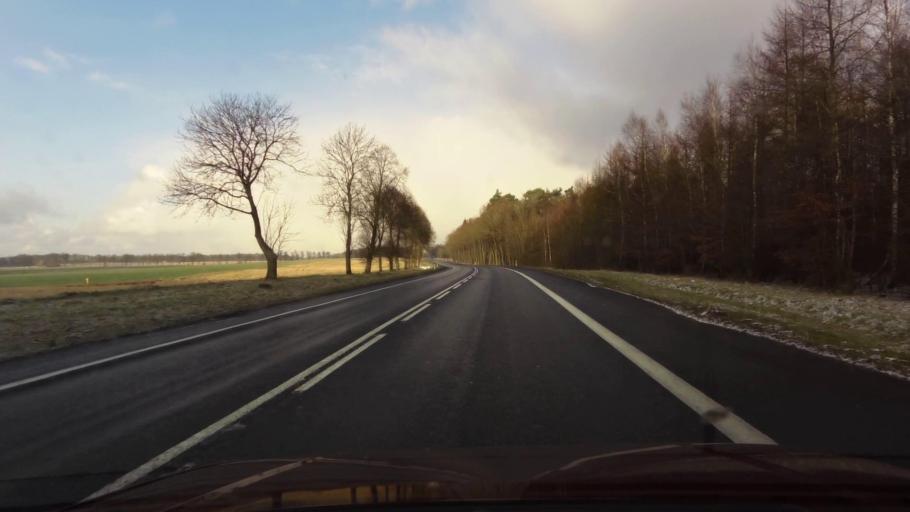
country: PL
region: West Pomeranian Voivodeship
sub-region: Powiat bialogardzki
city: Bialogard
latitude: 54.0904
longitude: 15.9903
